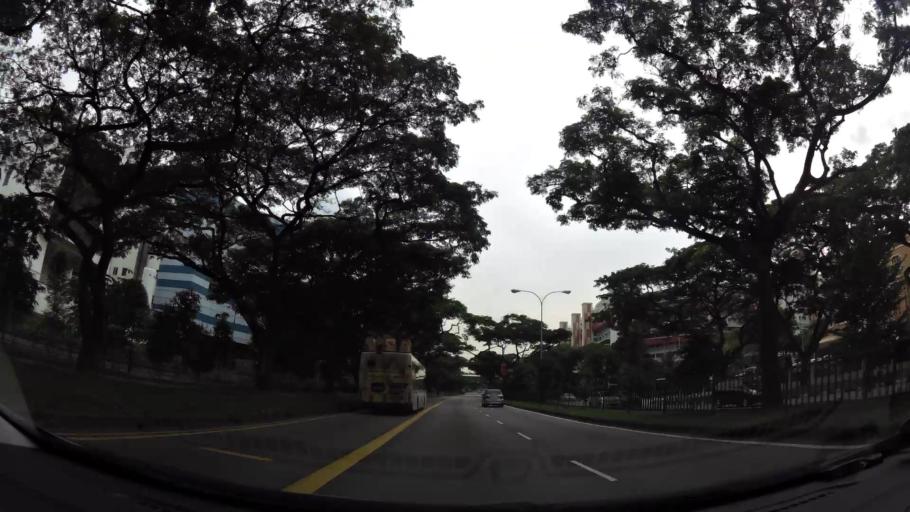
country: SG
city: Singapore
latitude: 1.3561
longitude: 103.8923
